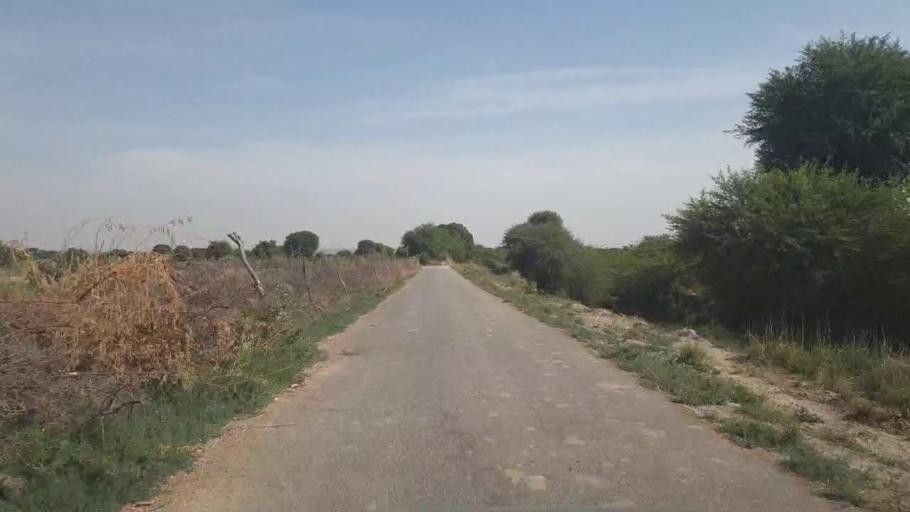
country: PK
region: Sindh
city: Kunri
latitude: 25.1851
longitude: 69.6887
